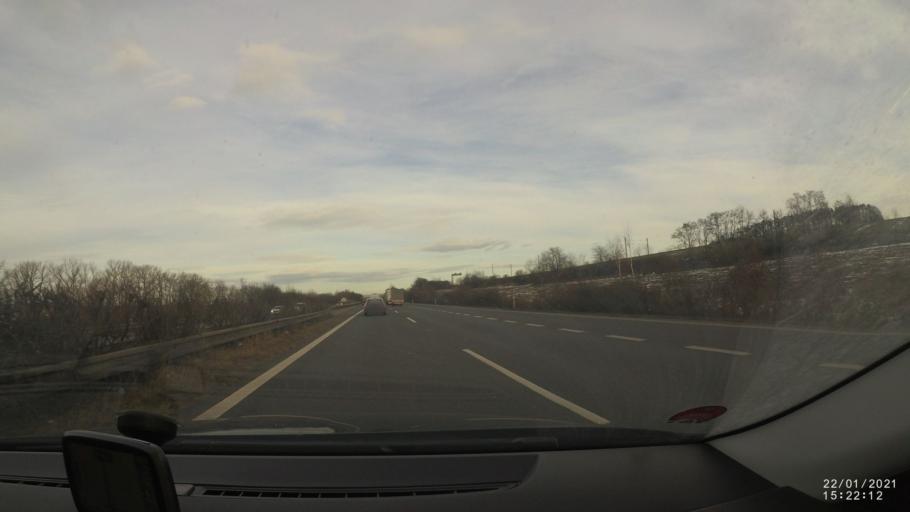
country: CZ
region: Plzensky
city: Zbiroh
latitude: 49.8412
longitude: 13.8182
